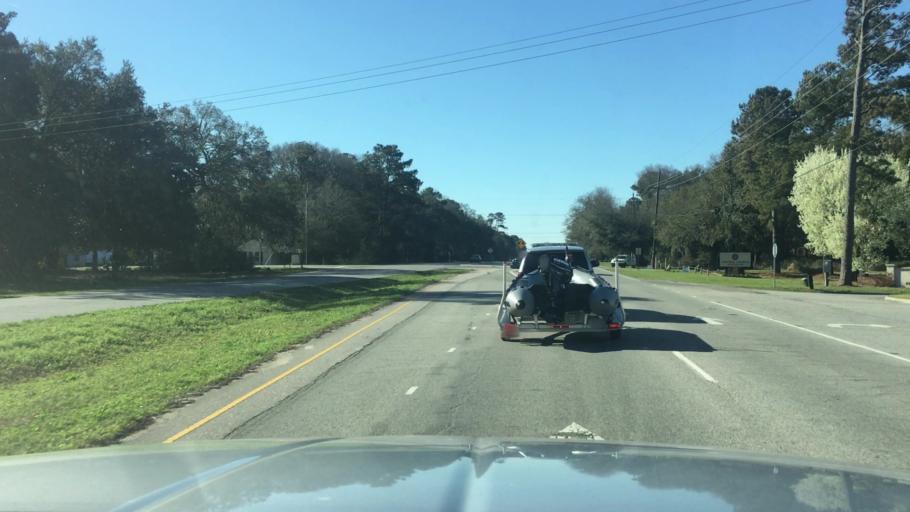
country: US
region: North Carolina
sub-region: New Hanover County
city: Sea Breeze
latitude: 34.0744
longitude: -77.8953
